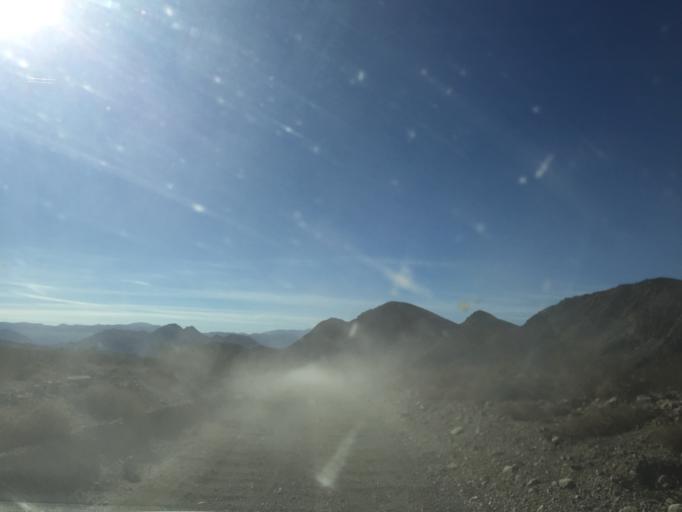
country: US
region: California
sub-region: Inyo County
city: Lone Pine
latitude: 36.7770
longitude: -117.5299
